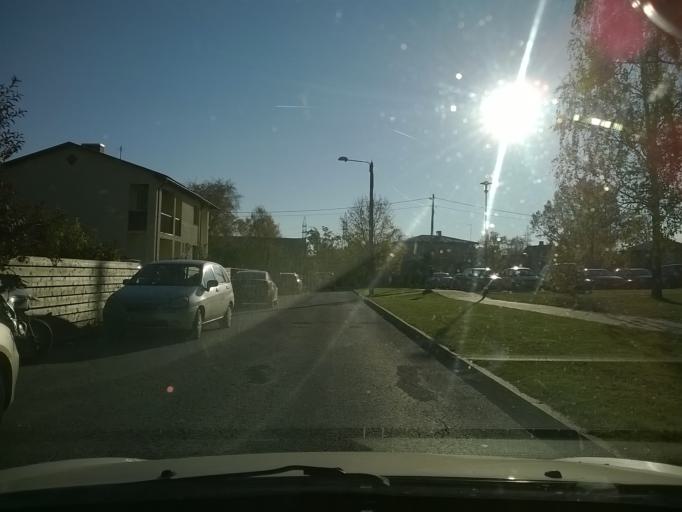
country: EE
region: Tartu
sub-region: Tartu linn
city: Tartu
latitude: 58.3490
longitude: 26.7155
